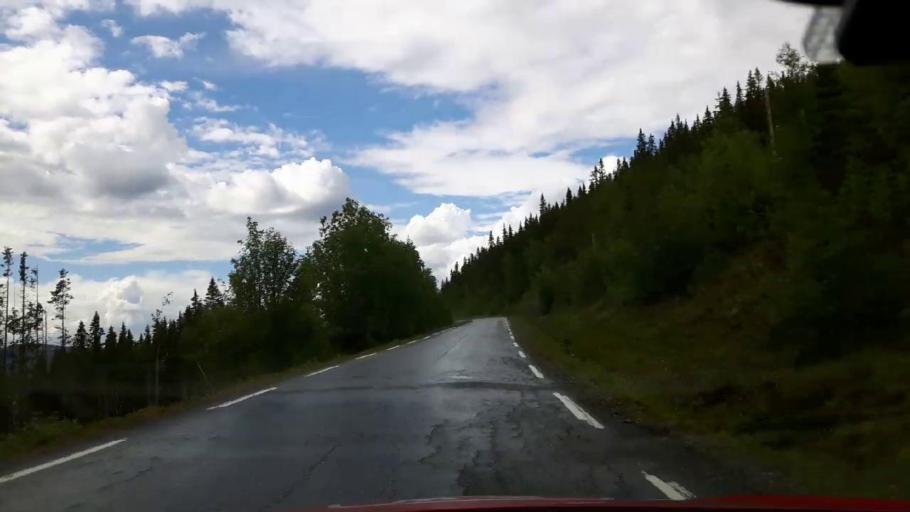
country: NO
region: Nord-Trondelag
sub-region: Lierne
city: Sandvika
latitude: 64.1026
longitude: 14.0003
